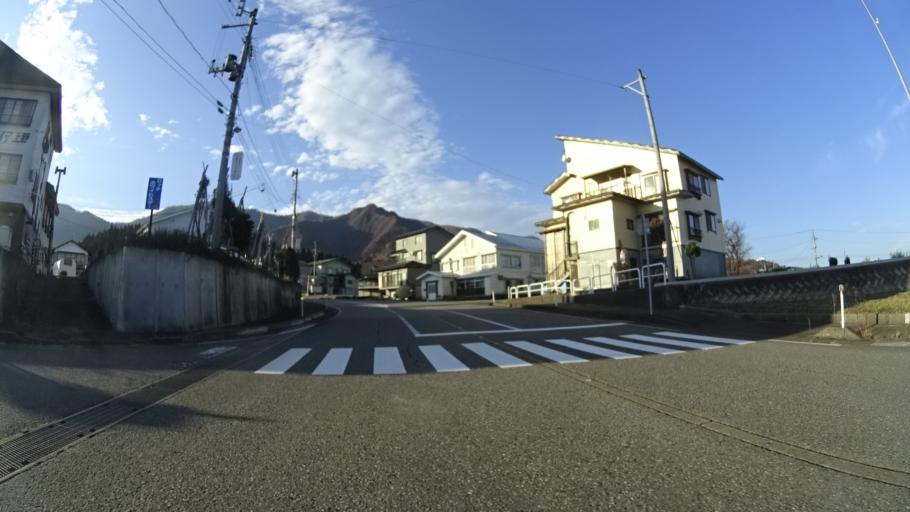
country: JP
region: Niigata
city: Shiozawa
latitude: 36.9872
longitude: 138.8010
